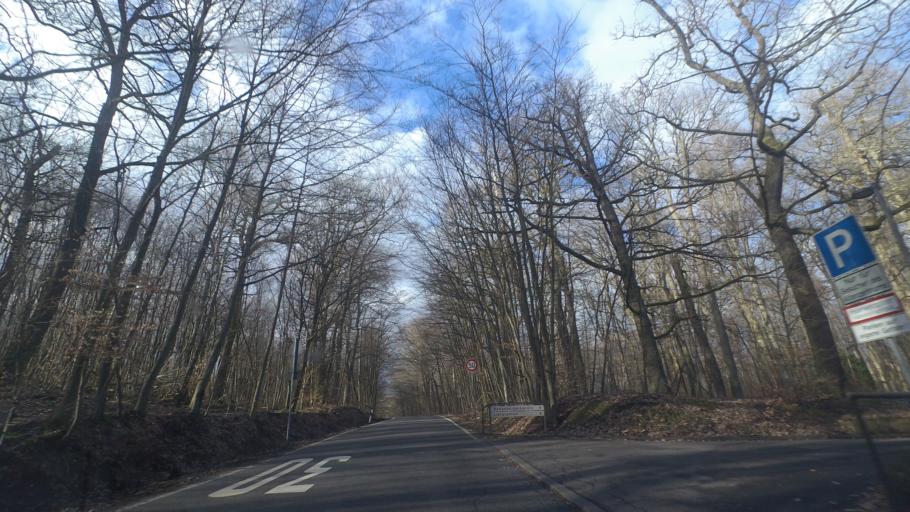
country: DE
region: Hesse
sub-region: Regierungsbezirk Darmstadt
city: Wiesbaden
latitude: 50.1069
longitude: 8.2425
